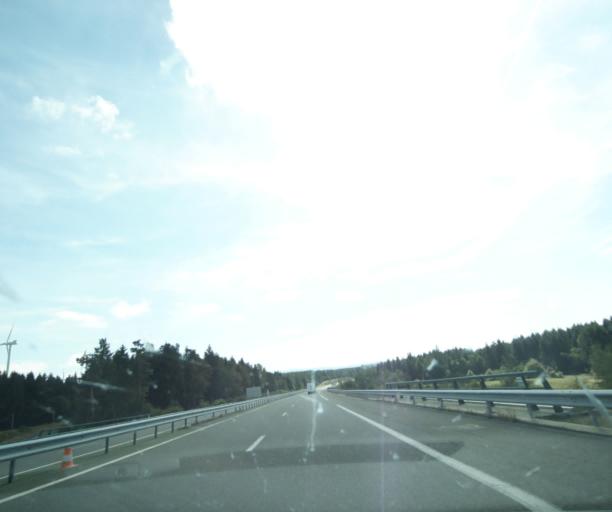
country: FR
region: Auvergne
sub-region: Departement du Puy-de-Dome
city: Saint-Sauves-d'Auvergne
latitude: 45.6913
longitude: 2.6956
